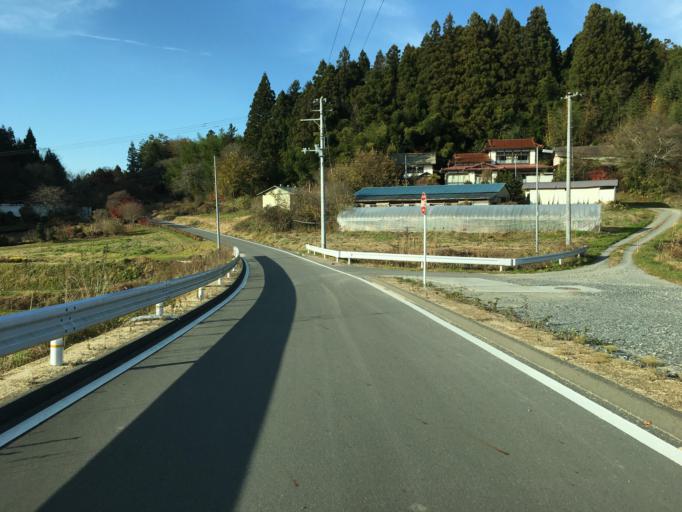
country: JP
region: Fukushima
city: Ishikawa
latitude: 37.2580
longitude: 140.5694
